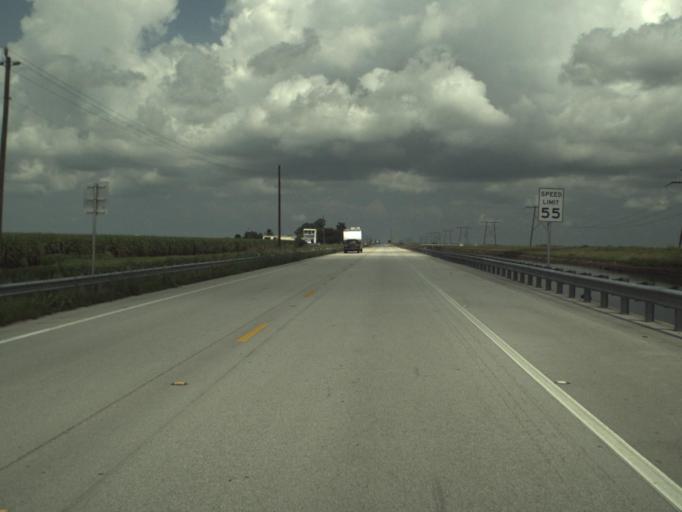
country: US
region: Florida
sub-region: Palm Beach County
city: Pahokee
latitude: 26.7594
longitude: -80.4928
